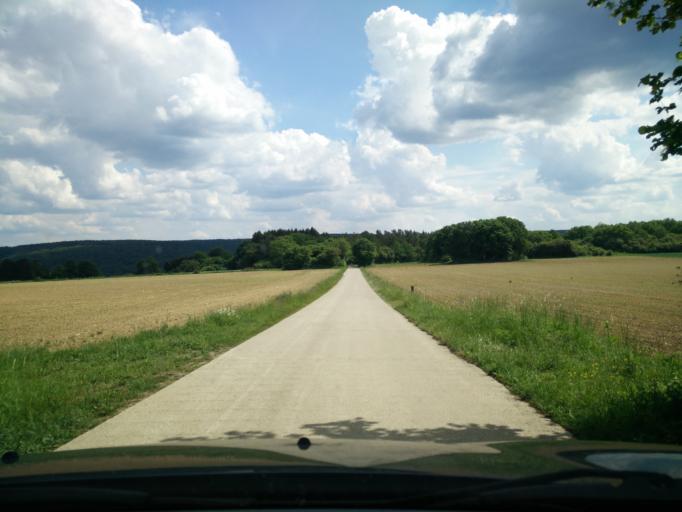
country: FR
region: Champagne-Ardenne
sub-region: Departement des Ardennes
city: Vireux-Molhain
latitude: 50.0866
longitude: 4.6183
